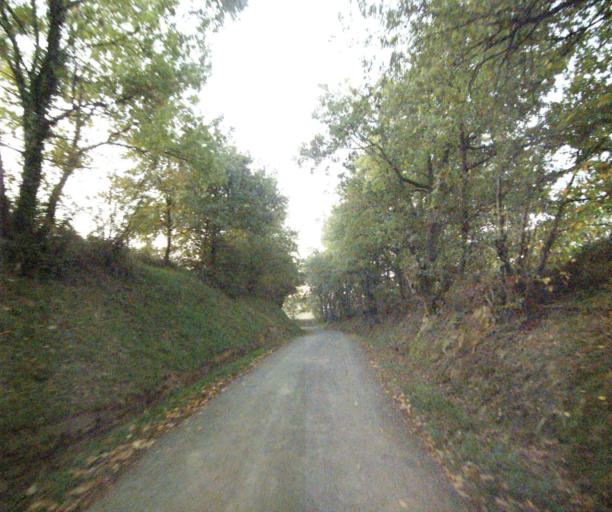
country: FR
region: Midi-Pyrenees
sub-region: Departement du Gers
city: Vic-Fezensac
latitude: 43.7780
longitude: 0.2267
